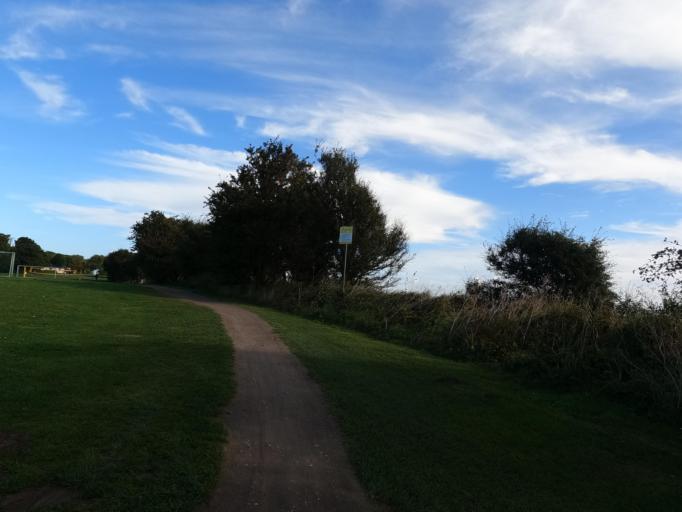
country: DE
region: Schleswig-Holstein
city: Dahme
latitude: 54.2637
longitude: 11.0820
